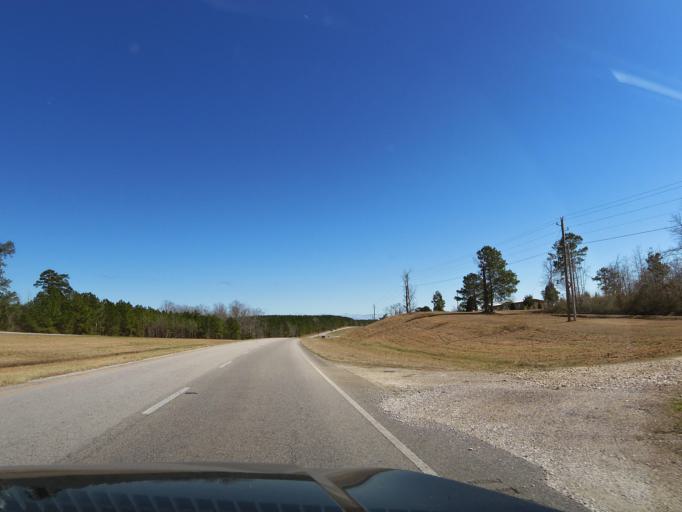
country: US
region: Alabama
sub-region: Bullock County
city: Union Springs
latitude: 32.1462
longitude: -85.6256
